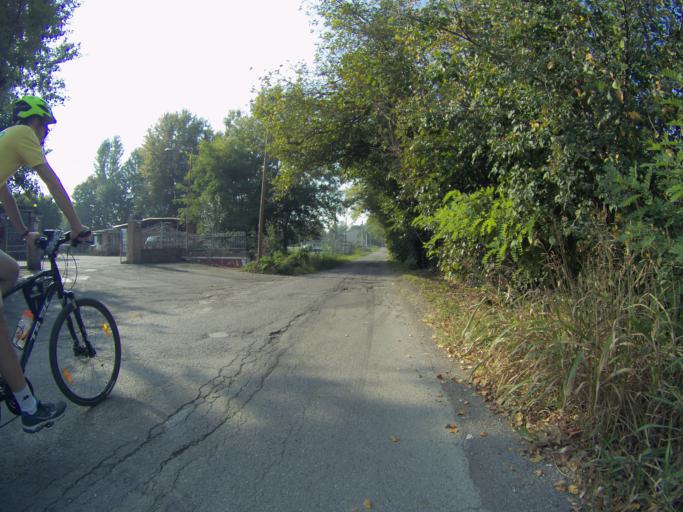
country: IT
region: Emilia-Romagna
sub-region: Provincia di Reggio Emilia
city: Forche
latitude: 44.6529
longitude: 10.5662
